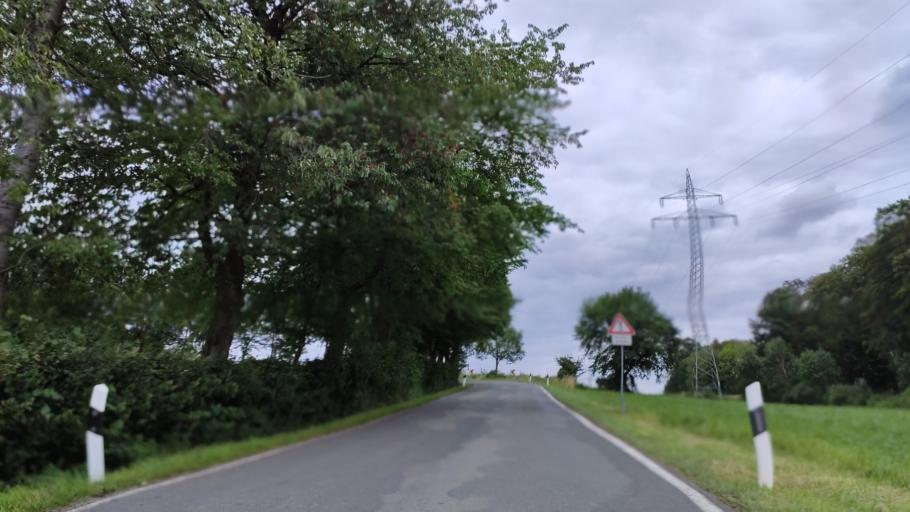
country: DE
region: North Rhine-Westphalia
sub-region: Regierungsbezirk Detmold
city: Nieheim
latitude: 51.7575
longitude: 9.0783
